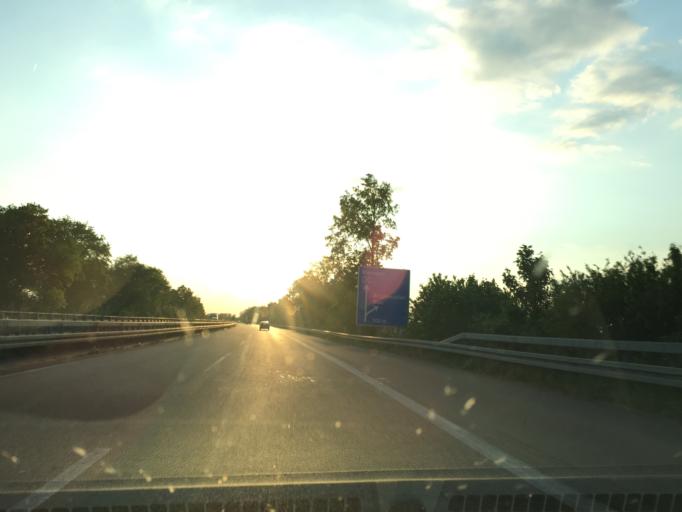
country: DE
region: North Rhine-Westphalia
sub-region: Regierungsbezirk Detmold
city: Rodinghausen
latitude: 52.1965
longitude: 8.4792
